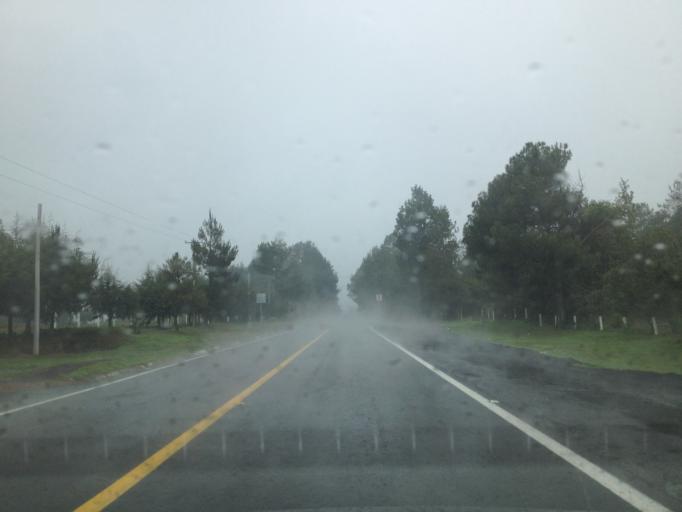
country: MX
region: Michoacan
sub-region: Patzcuaro
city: Santa Maria Huiramangaro (San Juan Tumbio)
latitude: 19.4893
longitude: -101.8010
